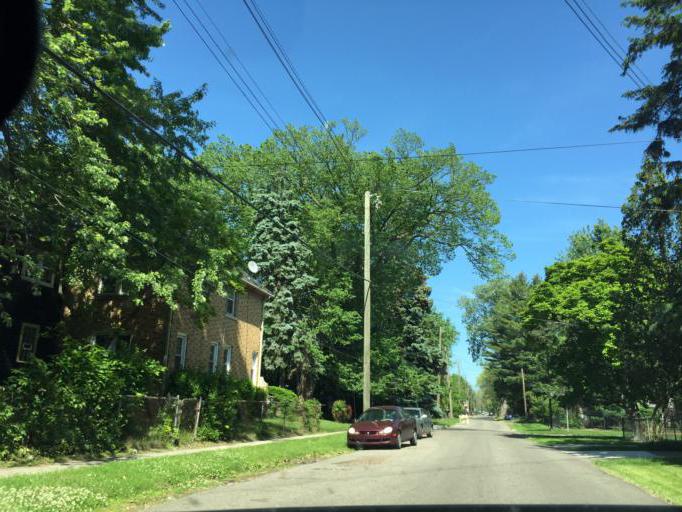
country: US
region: Michigan
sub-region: Oakland County
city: Southfield
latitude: 42.4098
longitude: -83.2347
